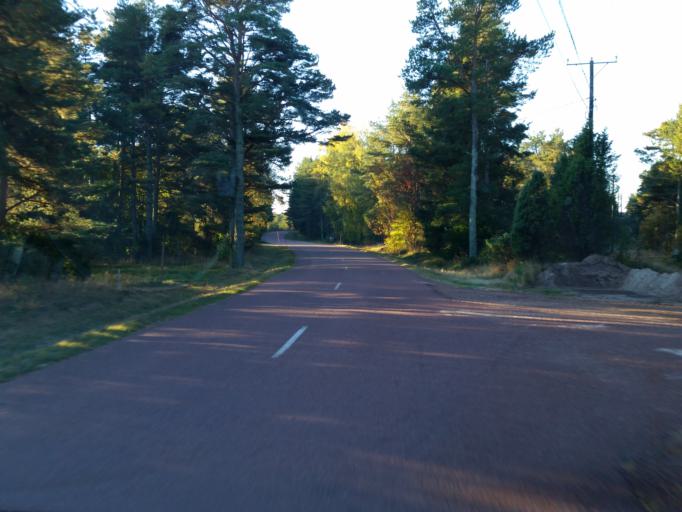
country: AX
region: Alands skaergard
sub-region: Vardoe
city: Vardoe
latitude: 60.2787
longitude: 20.3894
